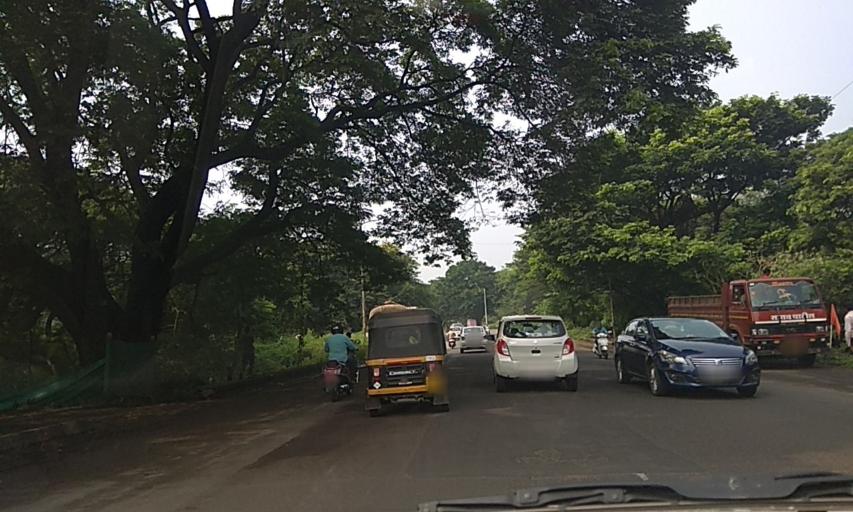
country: IN
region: Maharashtra
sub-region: Pune Division
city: Khadki
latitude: 18.5534
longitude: 73.8577
